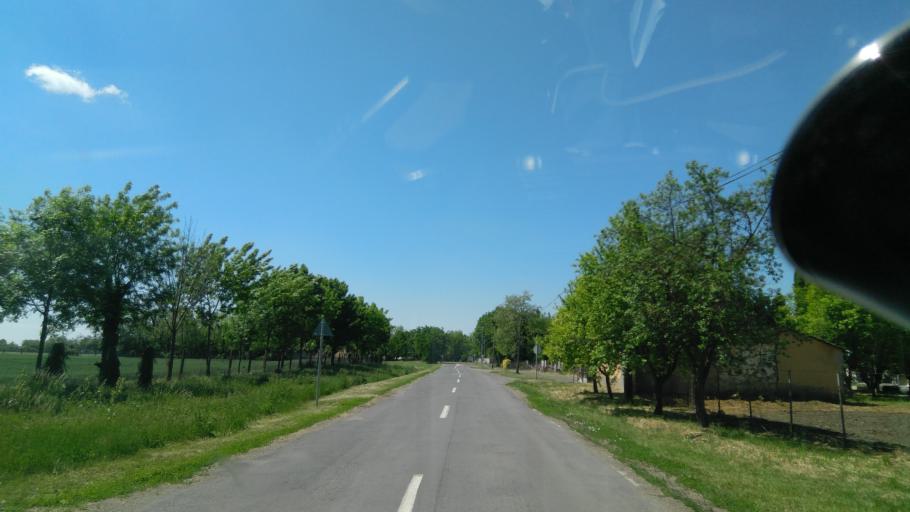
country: HU
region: Bekes
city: Kunagota
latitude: 46.4308
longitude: 21.0611
